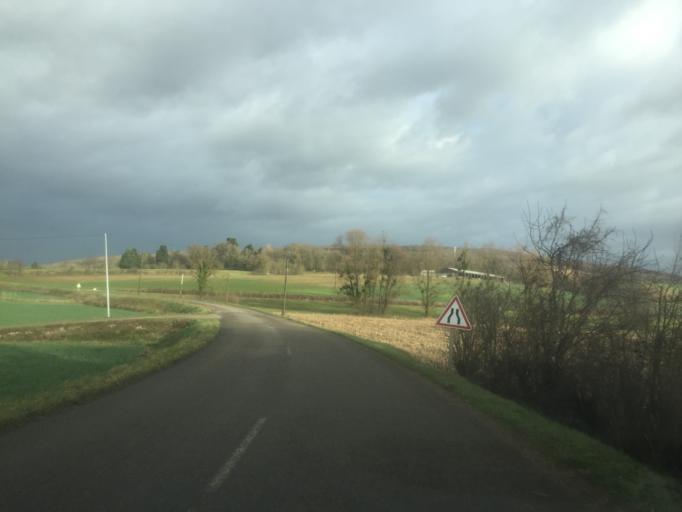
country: FR
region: Franche-Comte
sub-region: Departement du Jura
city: Orchamps
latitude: 47.2173
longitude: 5.6809
